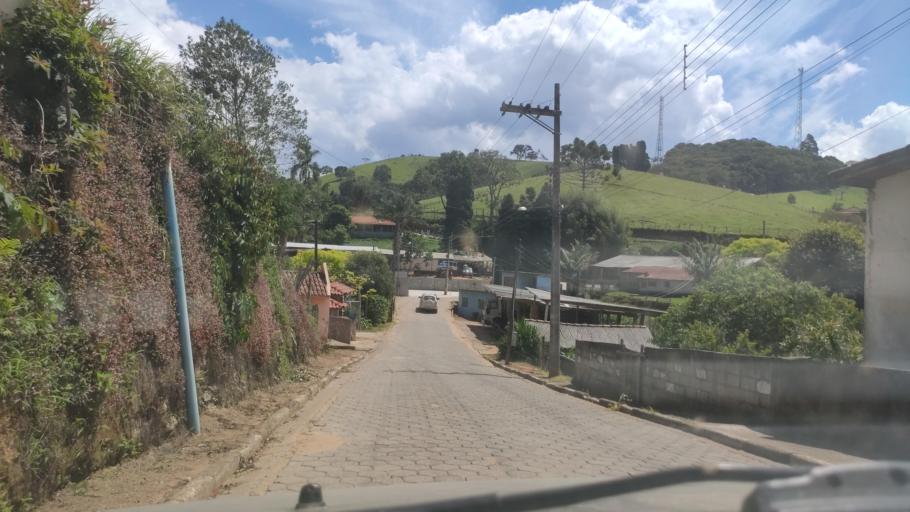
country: BR
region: Minas Gerais
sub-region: Cambui
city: Cambui
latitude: -22.7070
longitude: -46.0351
